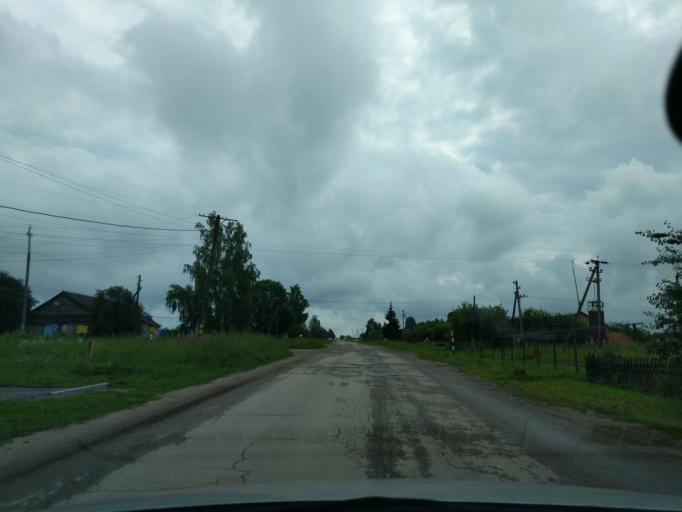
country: RU
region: Kaluga
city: Myatlevo
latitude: 54.7966
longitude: 35.7395
